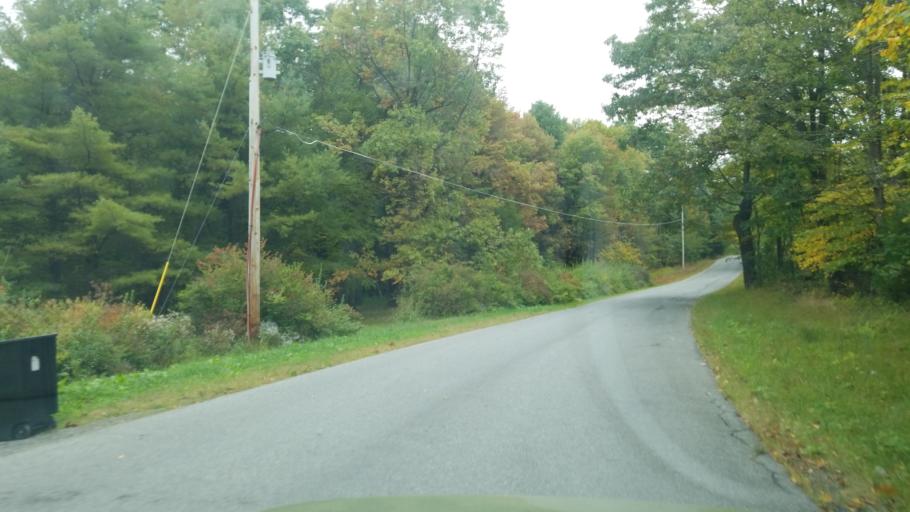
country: US
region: Pennsylvania
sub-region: Clearfield County
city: Curwensville
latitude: 41.0113
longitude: -78.5466
